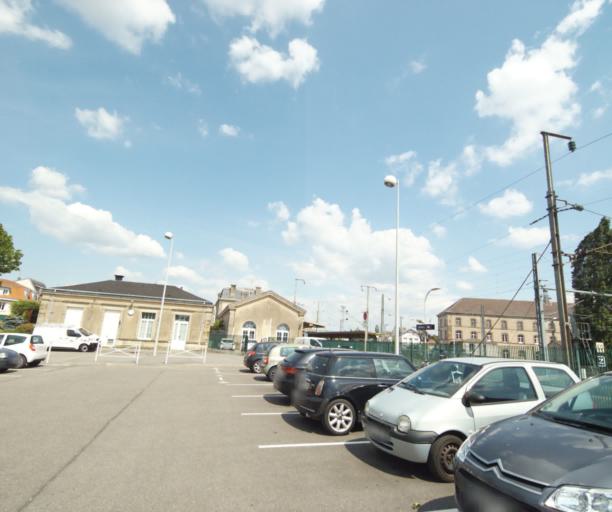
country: FR
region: Lorraine
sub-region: Departement de Meurthe-et-Moselle
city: Luneville
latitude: 48.5878
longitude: 6.4959
